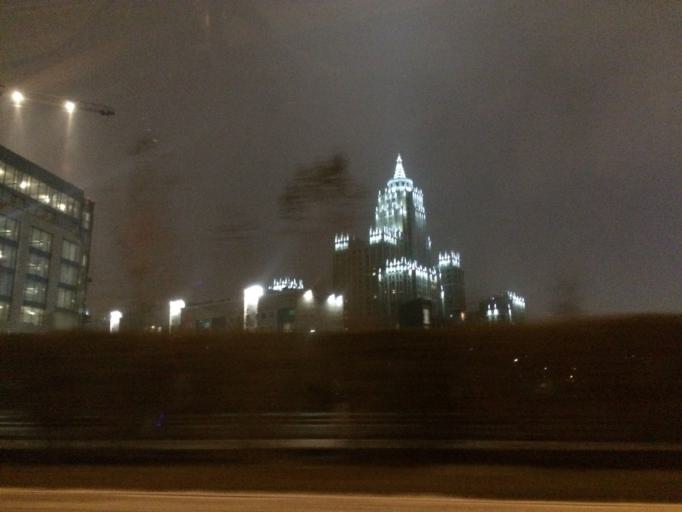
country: KZ
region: Astana Qalasy
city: Astana
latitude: 51.1408
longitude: 71.4101
